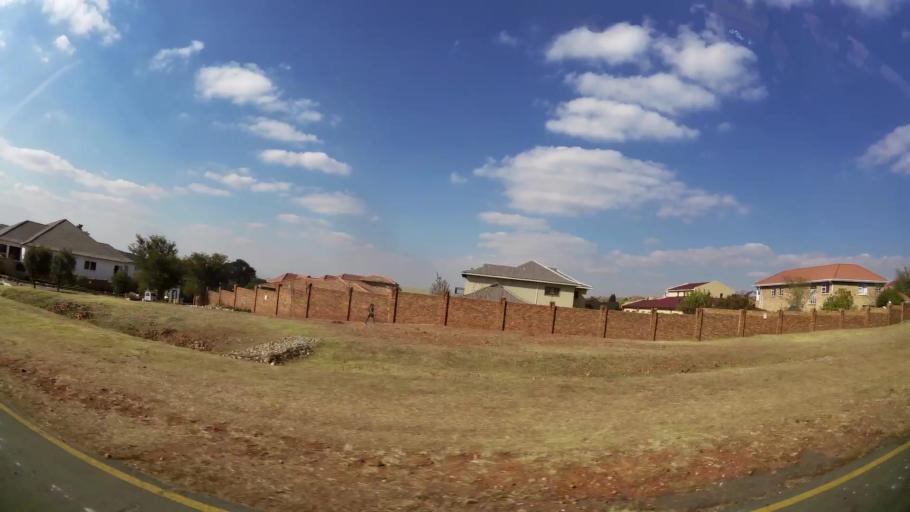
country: ZA
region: Gauteng
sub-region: West Rand District Municipality
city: Krugersdorp
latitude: -26.0549
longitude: 27.7543
